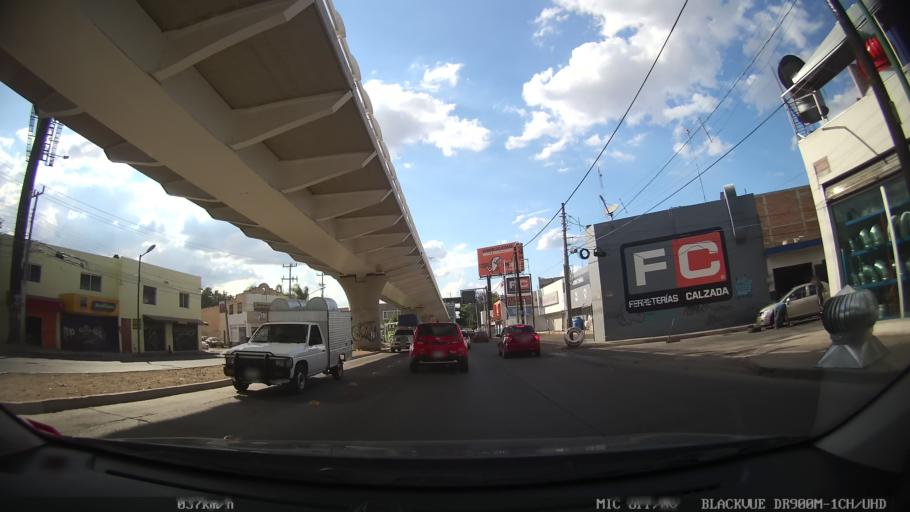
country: MX
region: Jalisco
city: Tlaquepaque
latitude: 20.6416
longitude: -103.3025
